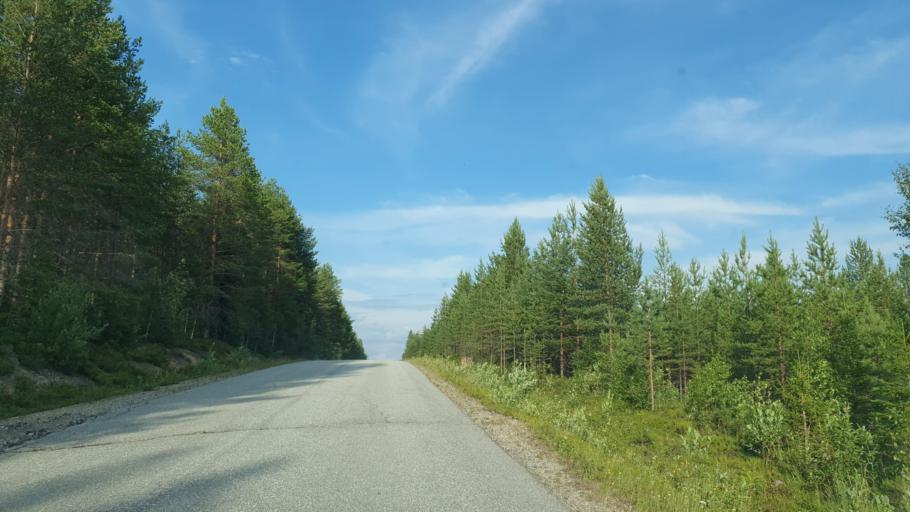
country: FI
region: Kainuu
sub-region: Kehys-Kainuu
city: Kuhmo
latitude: 64.3143
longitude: 29.5154
